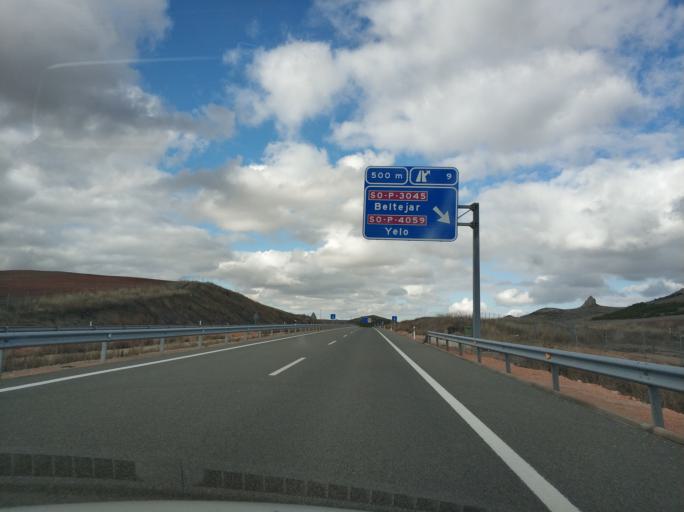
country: ES
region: Castille and Leon
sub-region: Provincia de Soria
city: Medinaceli
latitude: 41.2098
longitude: -2.4662
